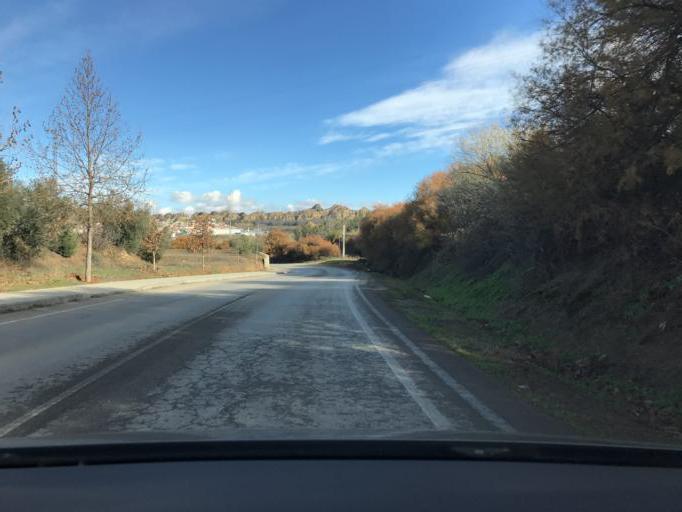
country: ES
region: Andalusia
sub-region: Provincia de Granada
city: Marchal
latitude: 37.3090
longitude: -3.2040
